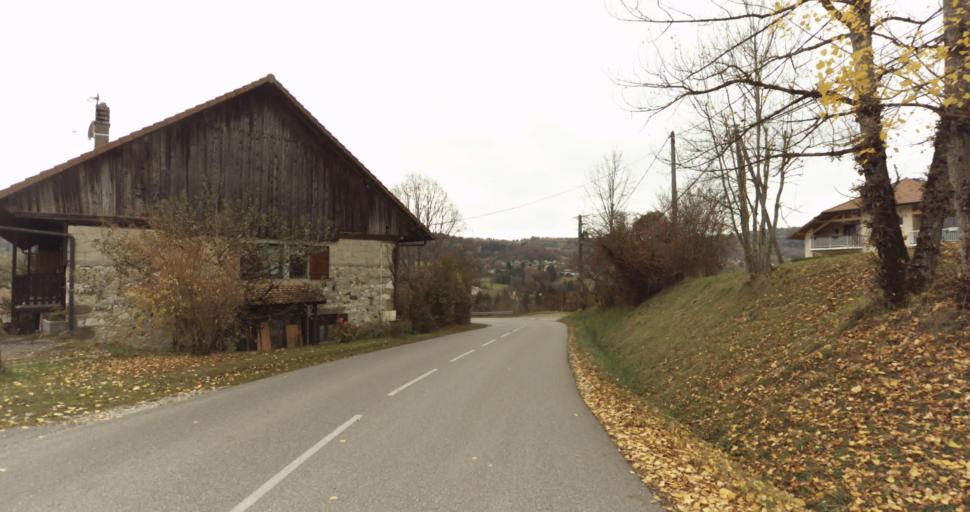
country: FR
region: Rhone-Alpes
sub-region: Departement de la Haute-Savoie
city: Saint-Martin-Bellevue
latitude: 45.9659
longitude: 6.1704
